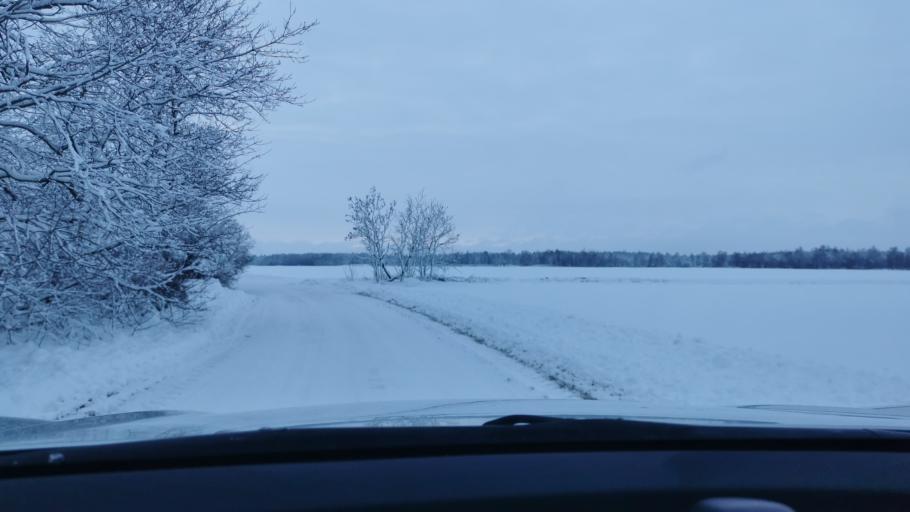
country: EE
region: Laeaene-Virumaa
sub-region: Someru vald
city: Someru
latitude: 59.4581
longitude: 26.4094
